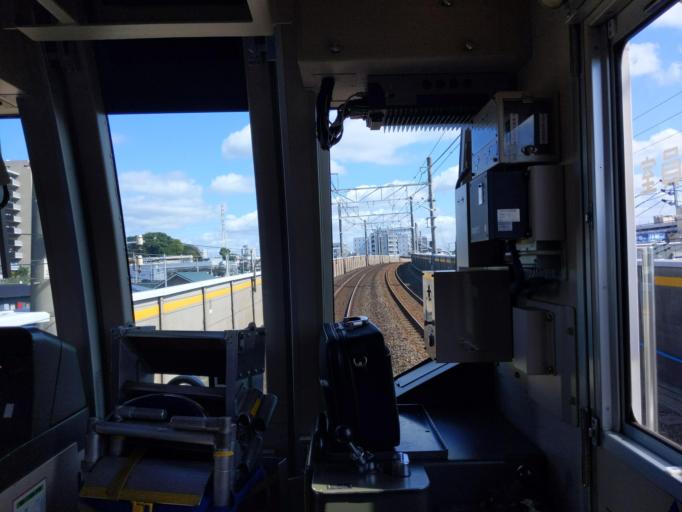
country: JP
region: Chiba
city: Shiroi
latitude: 35.7252
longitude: 140.1150
